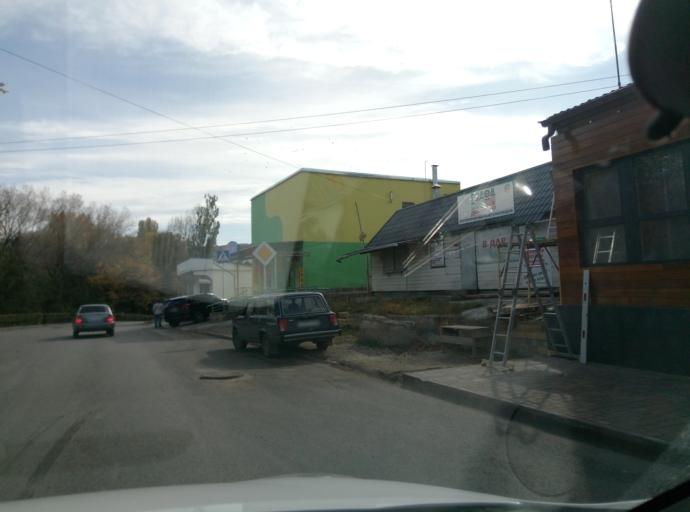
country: RU
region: Stavropol'skiy
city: Kislovodsk
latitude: 43.9175
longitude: 42.7020
